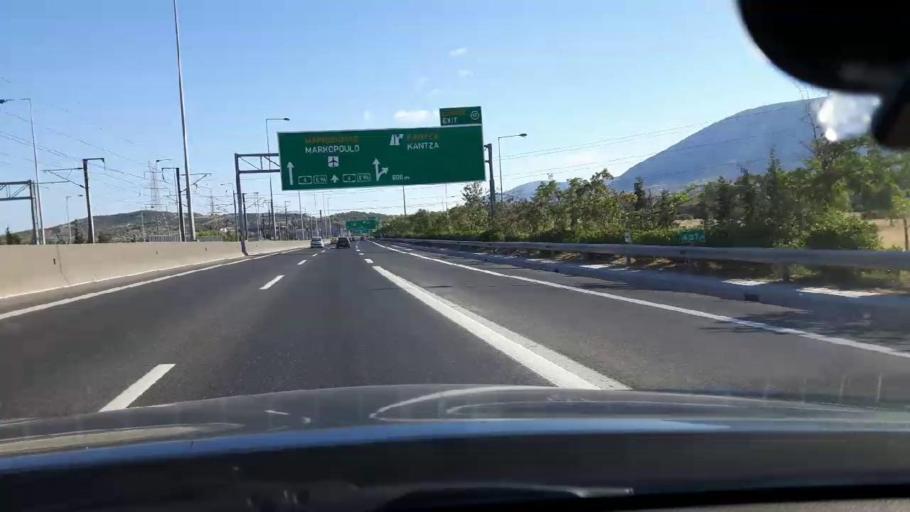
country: GR
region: Attica
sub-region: Nomarchia Anatolikis Attikis
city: Leondarion
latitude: 37.9805
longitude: 23.8699
